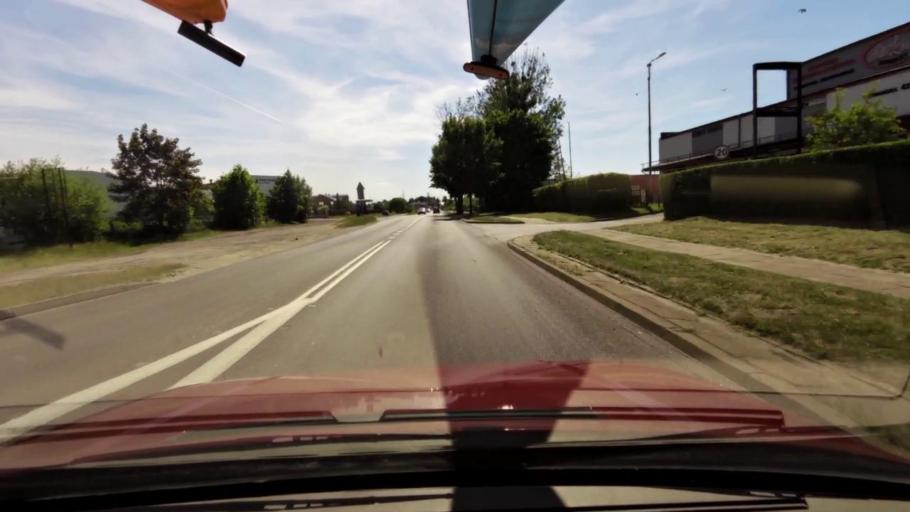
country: PL
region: Pomeranian Voivodeship
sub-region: Powiat slupski
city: Kobylnica
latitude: 54.4494
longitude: 17.0122
